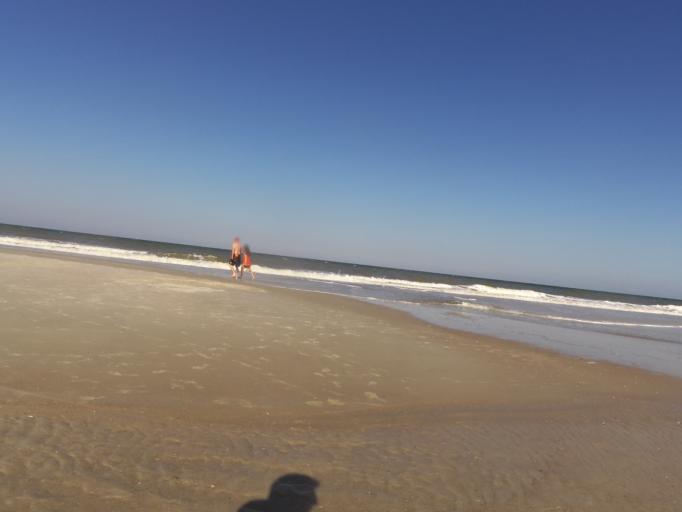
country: US
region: Florida
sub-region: Duval County
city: Atlantic Beach
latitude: 30.3405
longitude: -81.3957
